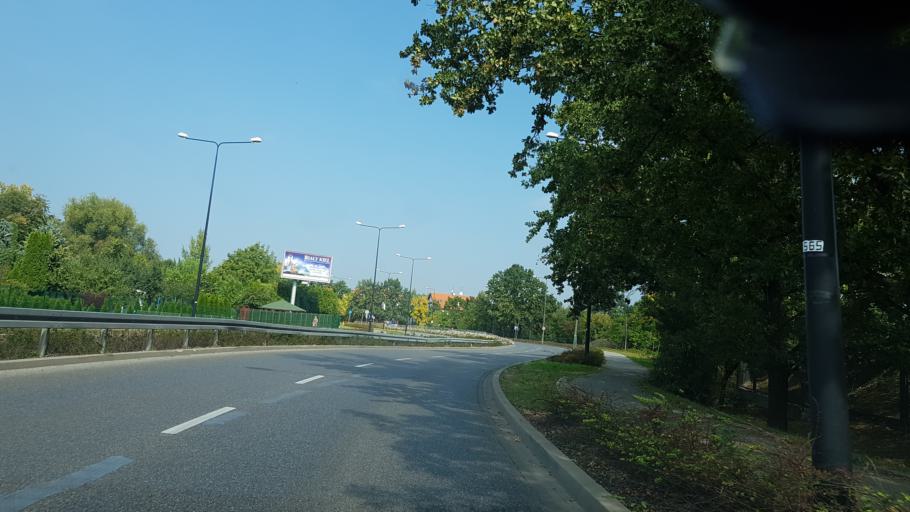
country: PL
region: Masovian Voivodeship
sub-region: Warszawa
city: Ursynow
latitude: 52.1658
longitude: 21.0450
